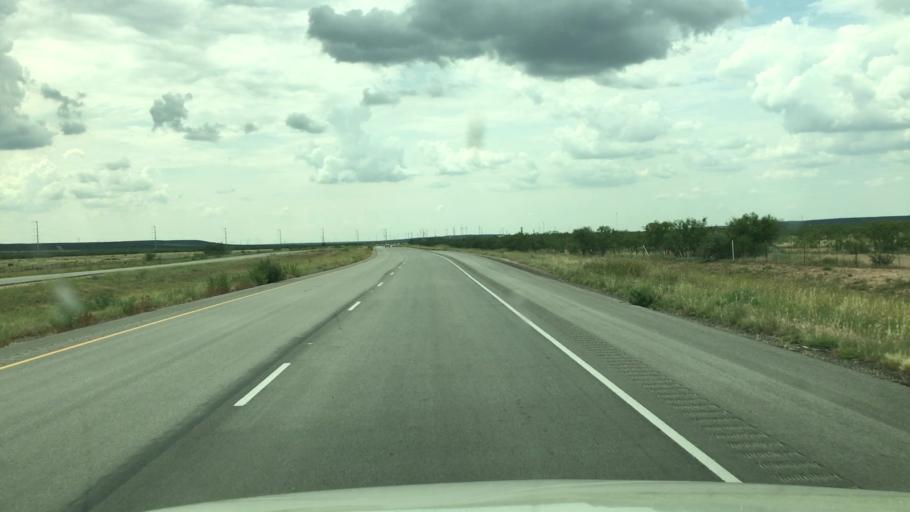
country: US
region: Texas
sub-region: Sterling County
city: Sterling City
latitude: 31.9617
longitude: -101.2155
